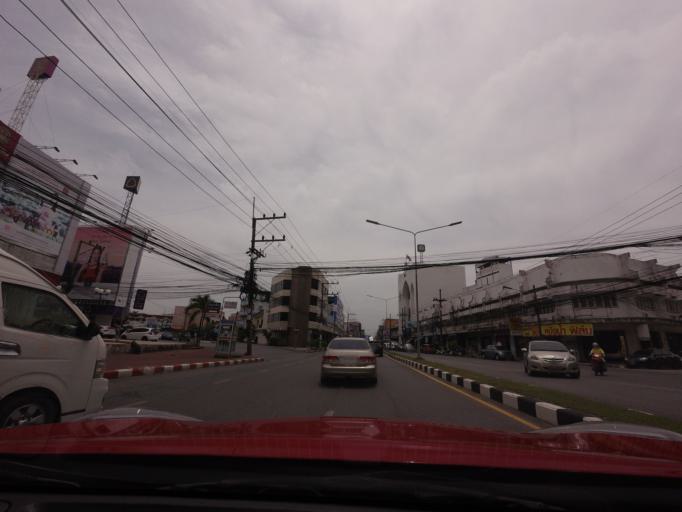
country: TH
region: Songkhla
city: Hat Yai
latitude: 6.9982
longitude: 100.4761
